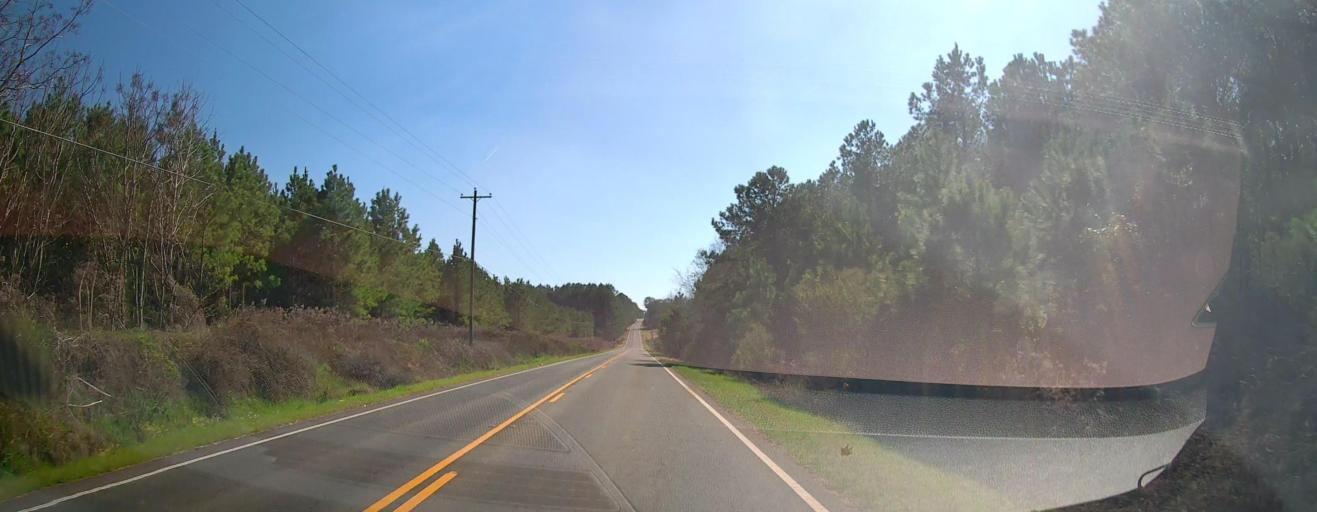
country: US
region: Georgia
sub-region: Macon County
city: Montezuma
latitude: 32.3258
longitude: -84.0224
